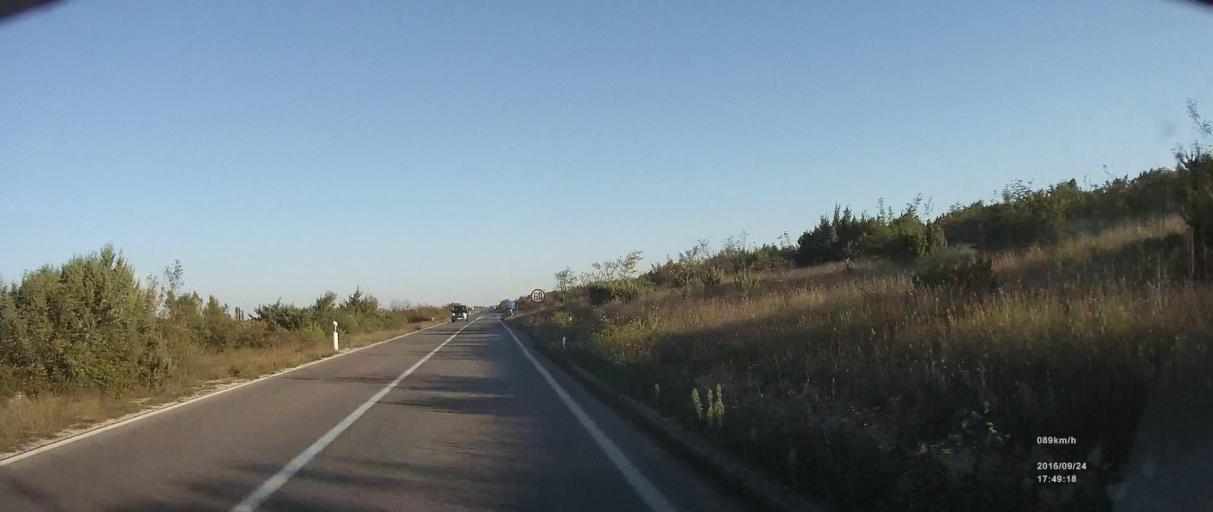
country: HR
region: Zadarska
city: Polaca
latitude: 44.0555
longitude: 15.5480
